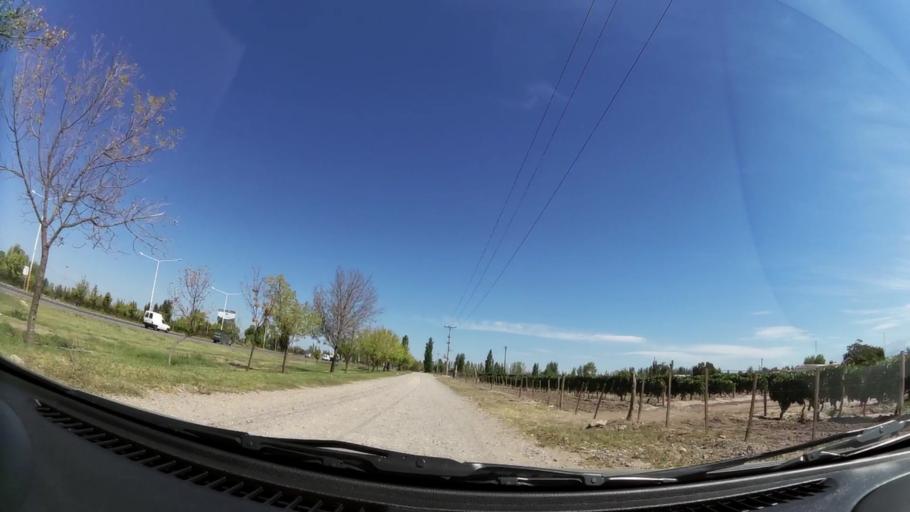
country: AR
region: Mendoza
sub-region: Departamento de Godoy Cruz
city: Godoy Cruz
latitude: -32.9794
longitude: -68.8482
